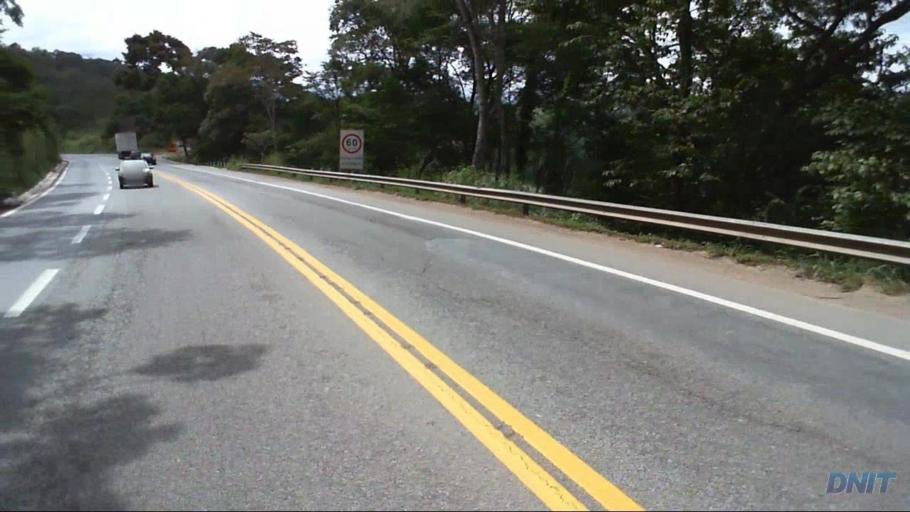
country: BR
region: Minas Gerais
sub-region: Caete
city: Caete
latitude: -19.7534
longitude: -43.6298
